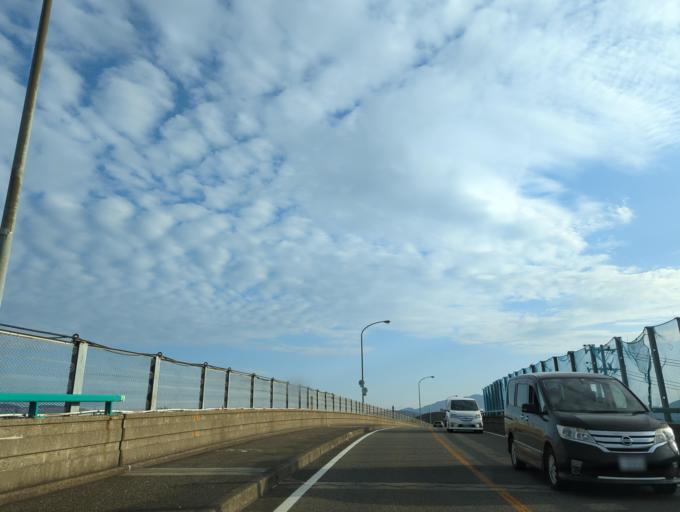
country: JP
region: Niigata
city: Kashiwazaki
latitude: 37.3657
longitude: 138.5630
